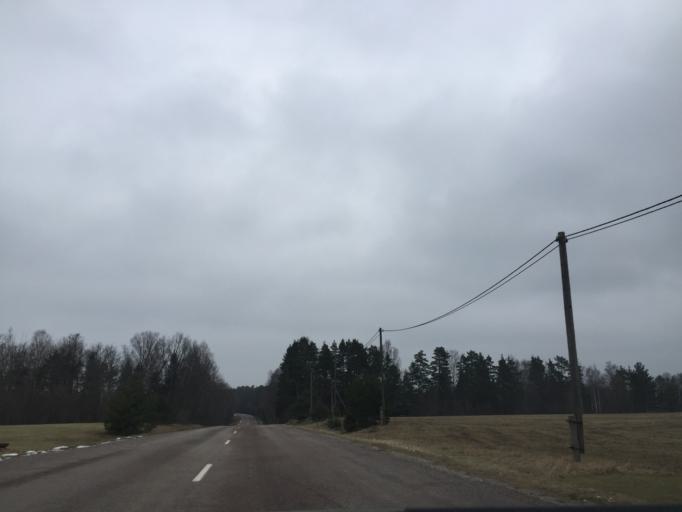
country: EE
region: Saare
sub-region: Kuressaare linn
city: Kuressaare
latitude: 58.3785
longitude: 22.2345
